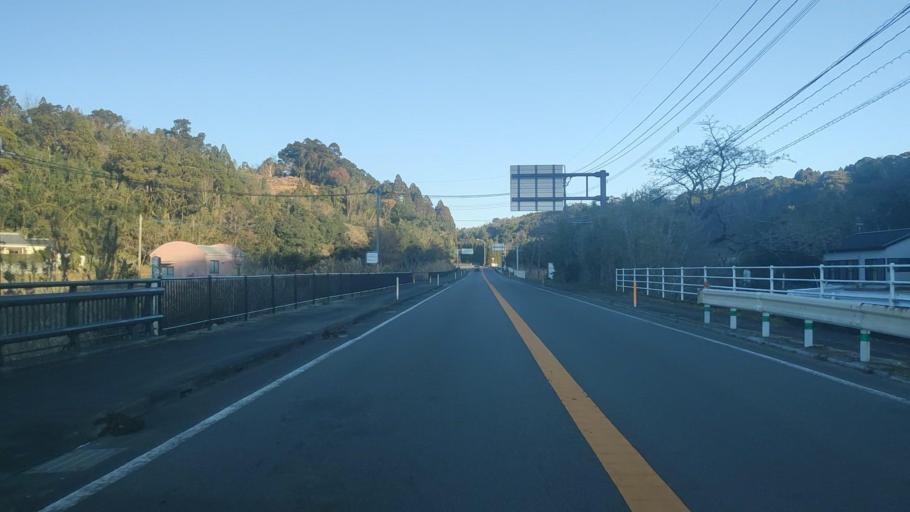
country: JP
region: Miyazaki
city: Takanabe
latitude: 32.1476
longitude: 131.5253
